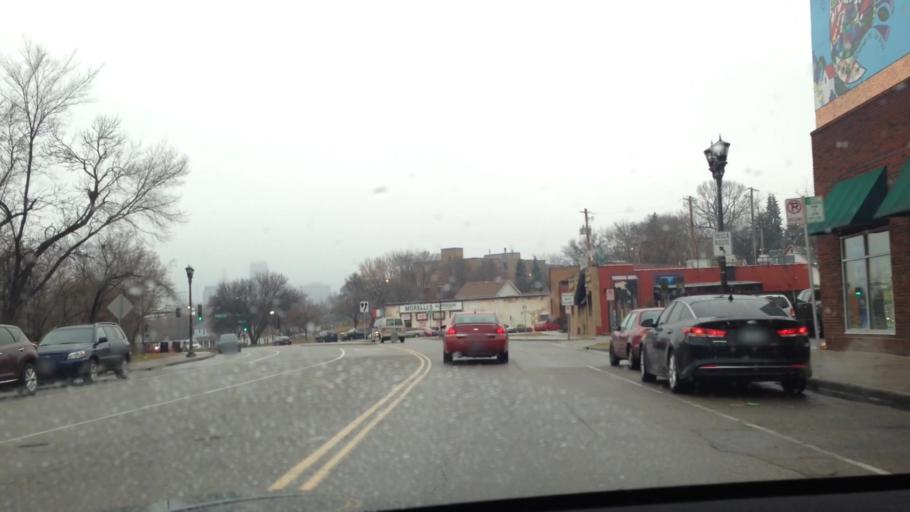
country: US
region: Minnesota
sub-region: Ramsey County
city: Saint Paul
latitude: 44.9612
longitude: -93.0765
